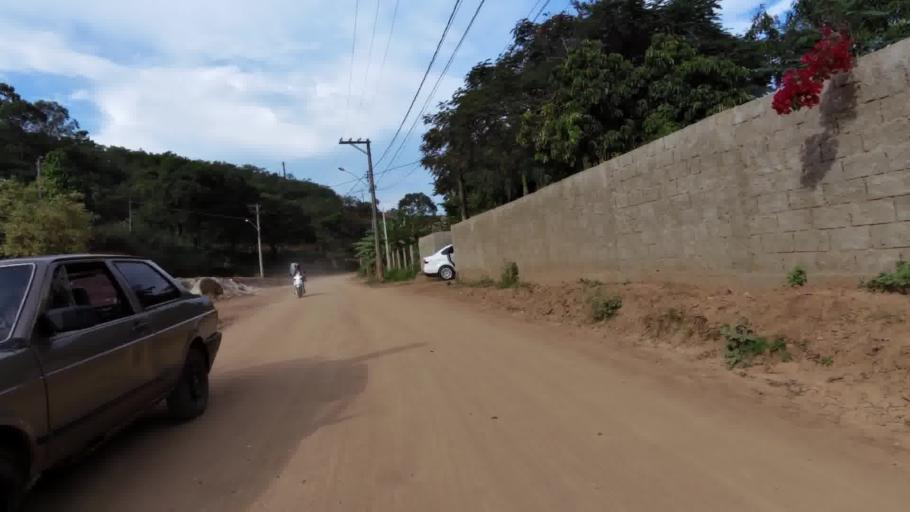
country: BR
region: Espirito Santo
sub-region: Piuma
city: Piuma
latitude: -20.8350
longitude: -40.7307
